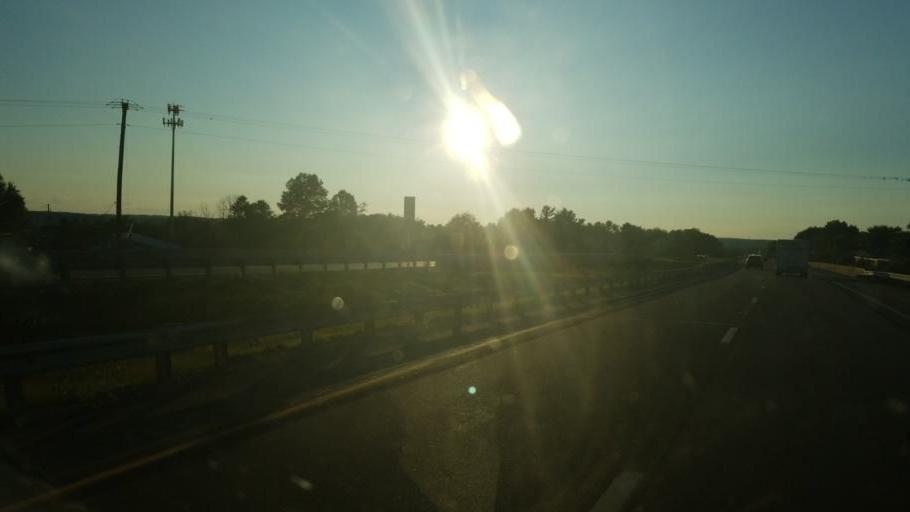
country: US
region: Ohio
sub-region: Mahoning County
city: Boardman
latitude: 40.9702
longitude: -80.6597
